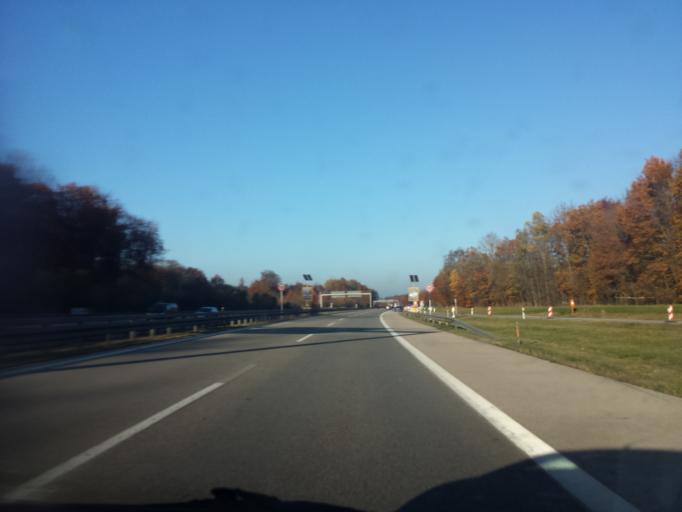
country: DE
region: Bavaria
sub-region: Upper Bavaria
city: Schaftlarn
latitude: 48.0218
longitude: 11.4200
